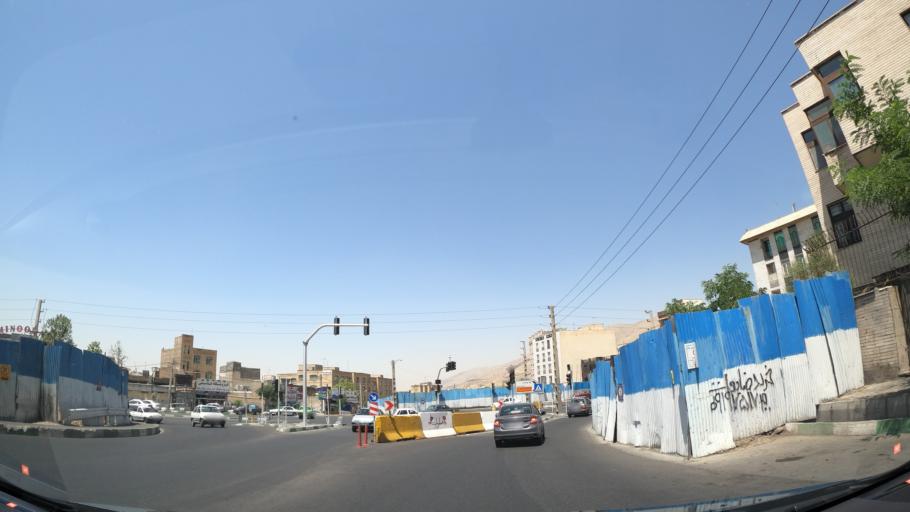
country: IR
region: Tehran
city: Tajrish
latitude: 35.7632
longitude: 51.2846
